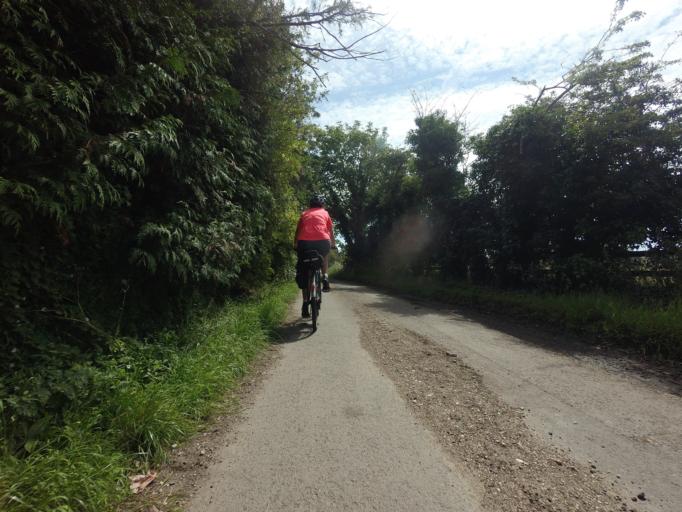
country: GB
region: England
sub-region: Kent
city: Stone
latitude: 51.0013
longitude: 0.8285
